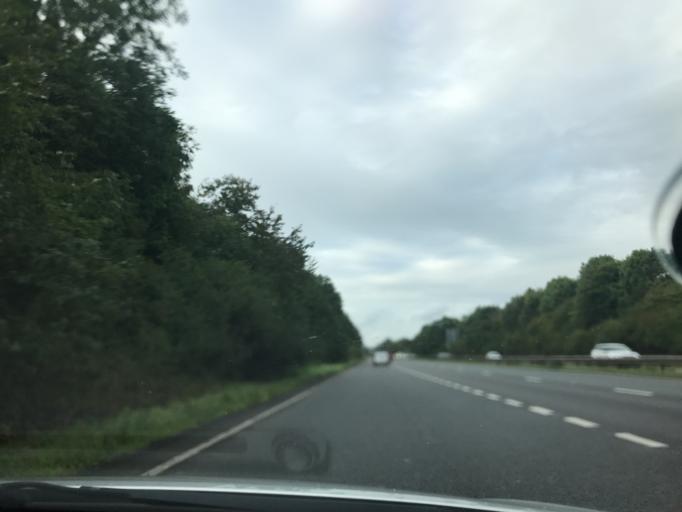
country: GB
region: England
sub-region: Cheshire West and Chester
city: Guilden Sutton
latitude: 53.1980
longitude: -2.8445
